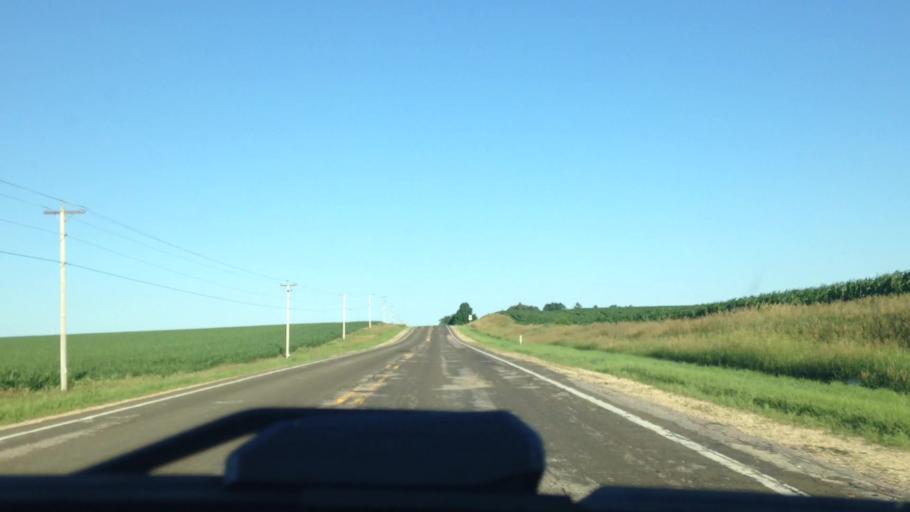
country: US
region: Wisconsin
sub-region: Columbia County
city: Poynette
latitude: 43.3378
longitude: -89.4161
